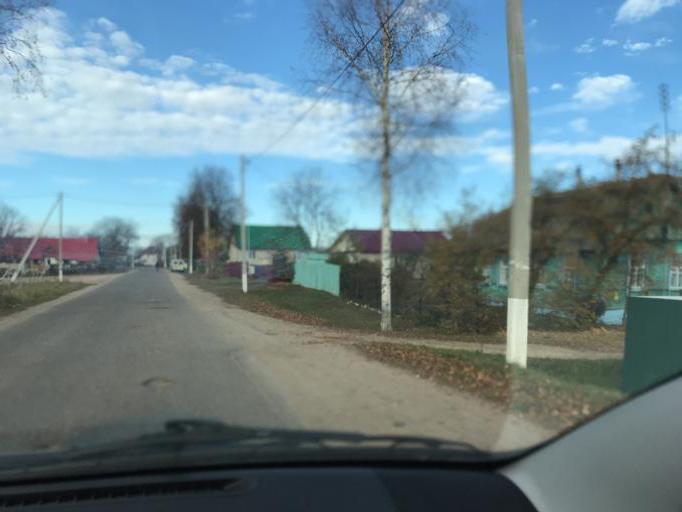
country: BY
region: Vitebsk
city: Haradok
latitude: 55.4609
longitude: 30.0034
